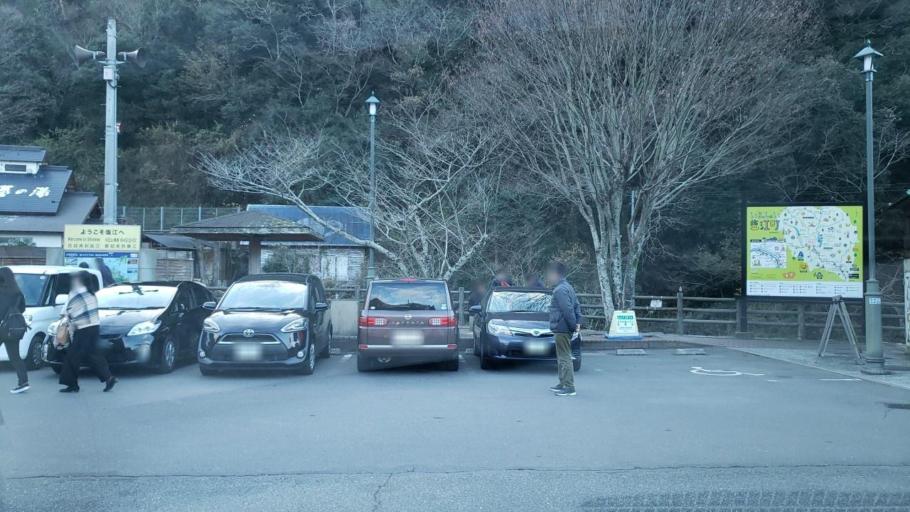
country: JP
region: Tokushima
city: Wakimachi
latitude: 34.1699
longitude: 134.0822
